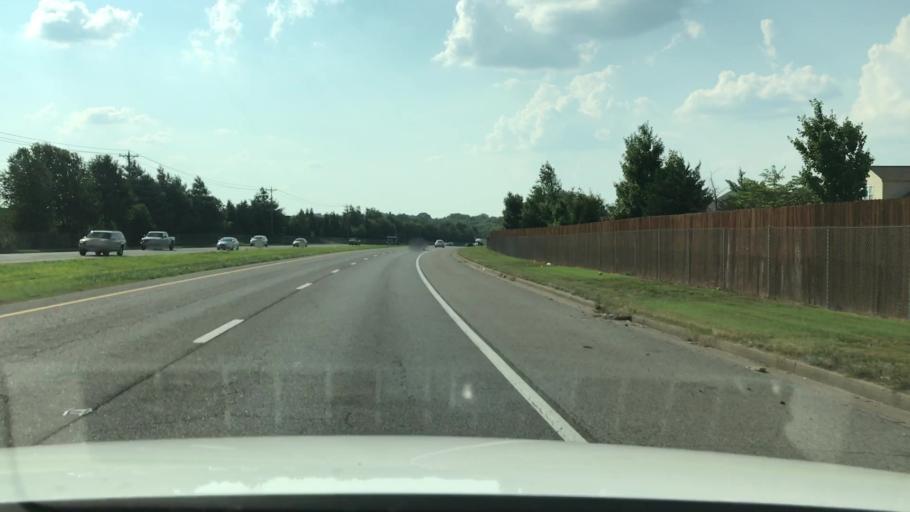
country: US
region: Tennessee
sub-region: Sumner County
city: Gallatin
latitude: 36.3645
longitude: -86.4549
